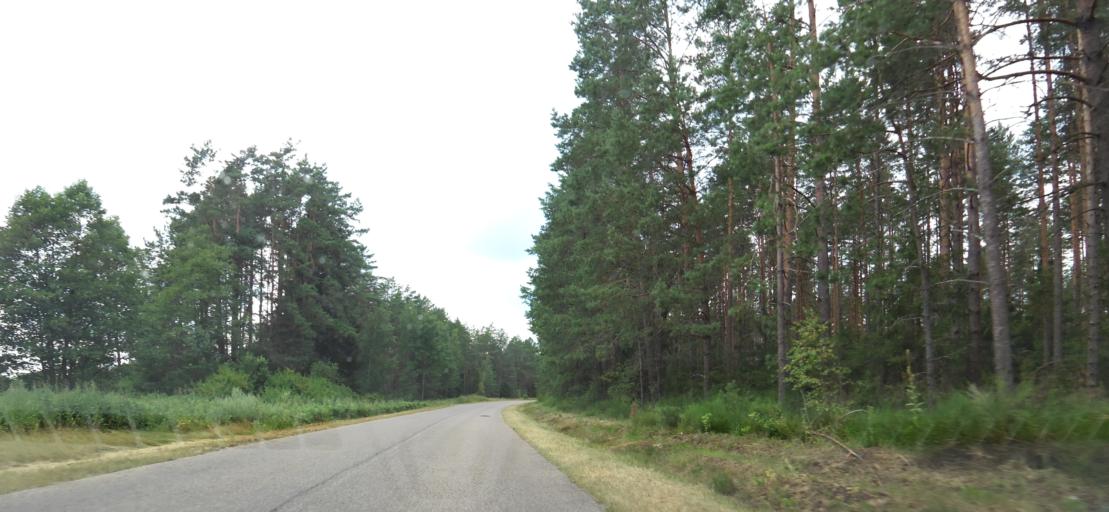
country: LT
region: Alytaus apskritis
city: Druskininkai
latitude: 53.9941
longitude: 24.0480
